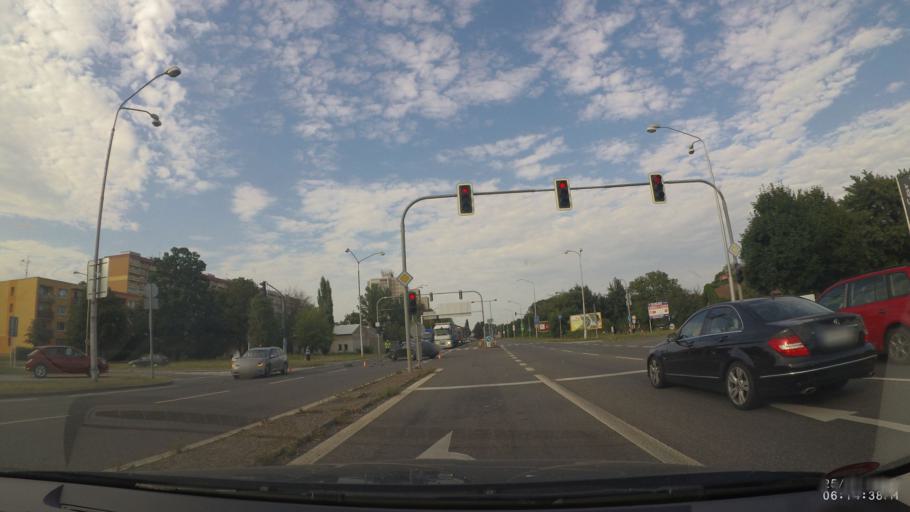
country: CZ
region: Kralovehradecky
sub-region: Okres Hradec Kralove
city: Hradec Kralove
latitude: 50.1963
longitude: 15.8137
